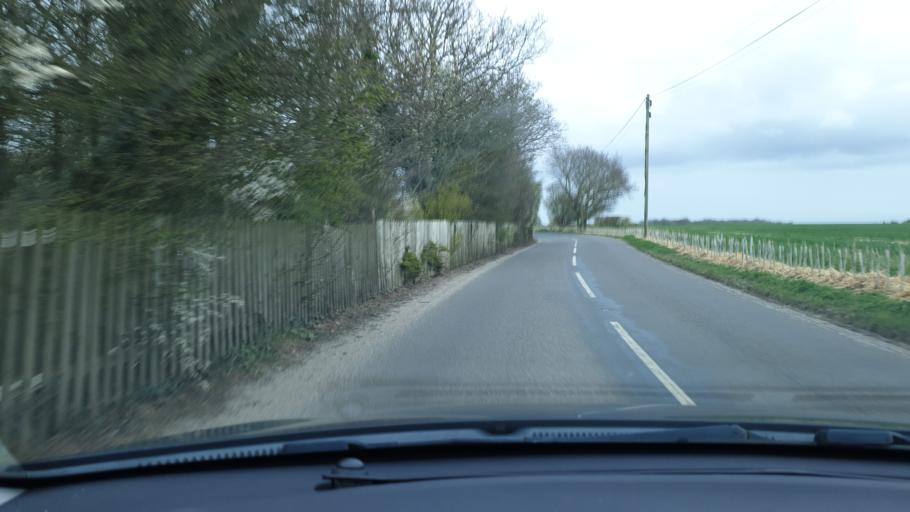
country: GB
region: England
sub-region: Essex
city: Mistley
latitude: 51.9085
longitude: 1.1267
